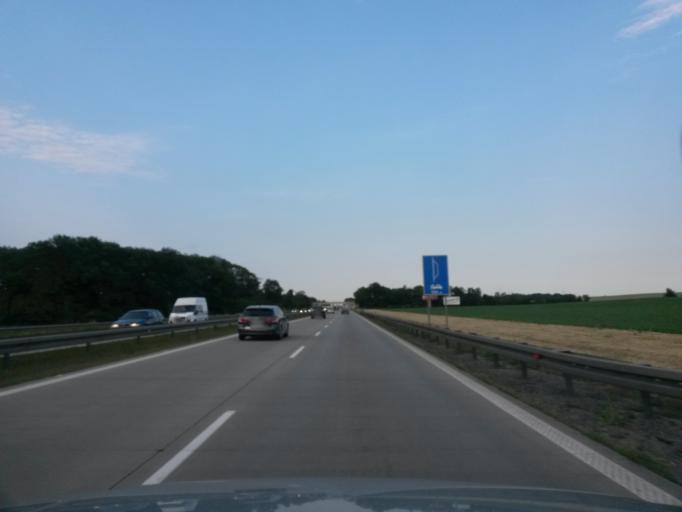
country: PL
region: Lower Silesian Voivodeship
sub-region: Powiat wroclawski
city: Gniechowice
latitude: 51.0349
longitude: 16.8477
